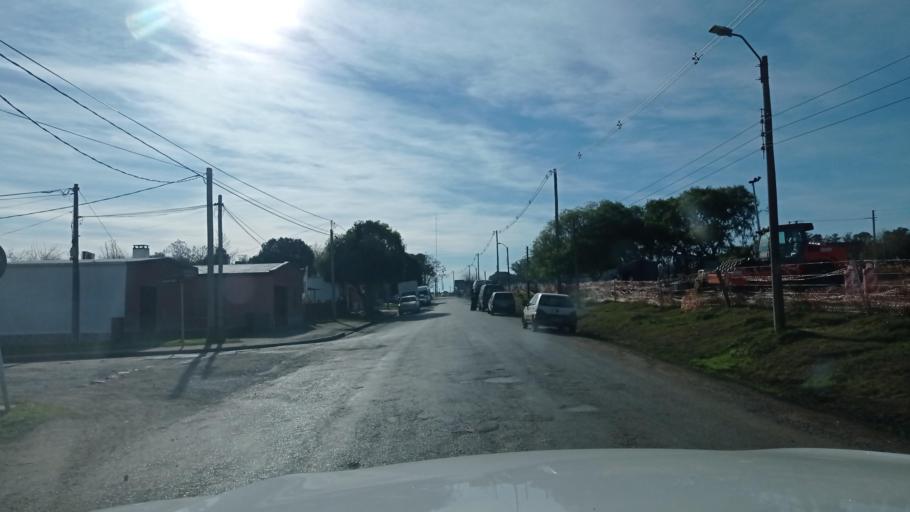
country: UY
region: Florida
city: Florida
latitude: -34.1015
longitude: -56.2398
